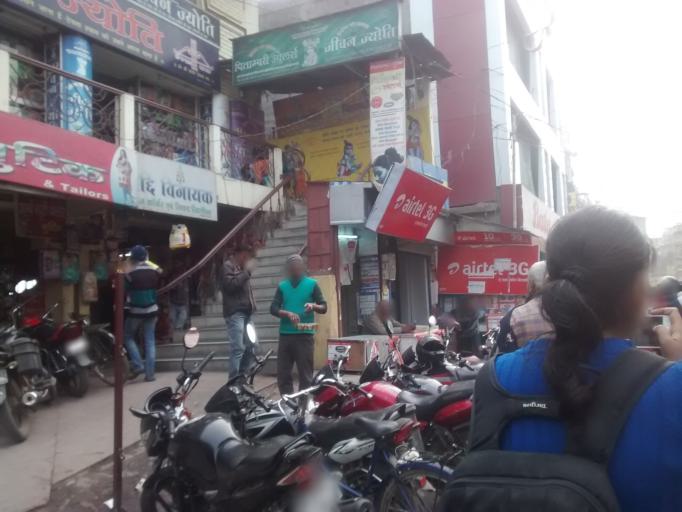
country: IN
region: Bihar
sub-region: Muzaffarpur
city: Muzaffarpur
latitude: 26.1196
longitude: 85.3910
